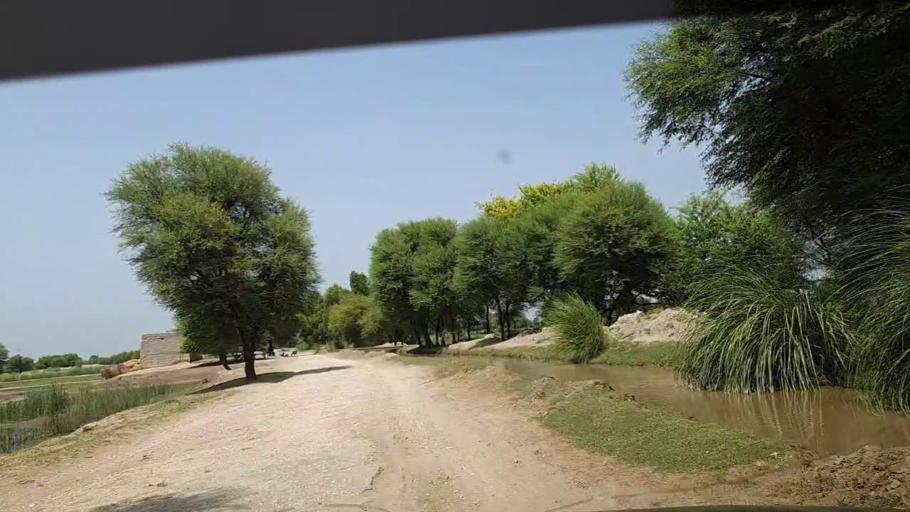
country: PK
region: Sindh
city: Khanpur
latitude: 27.8128
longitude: 69.4505
